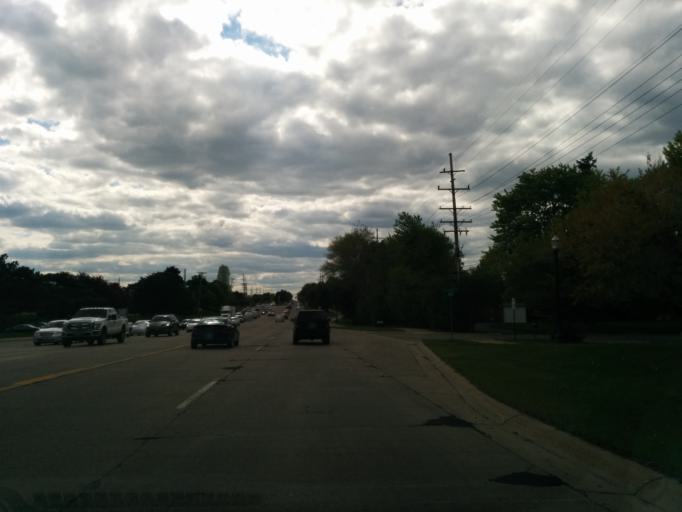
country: US
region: Michigan
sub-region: Oakland County
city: Farmington Hills
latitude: 42.4985
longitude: -83.3835
